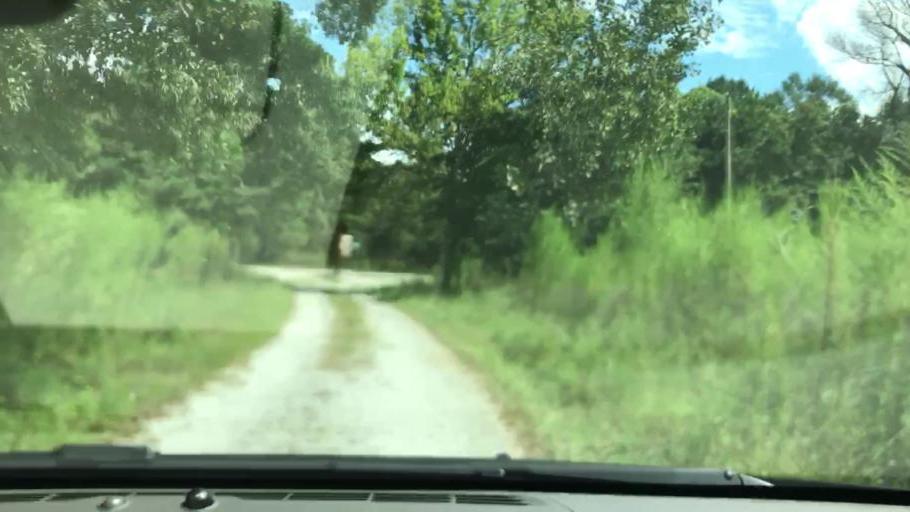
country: US
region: Georgia
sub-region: Quitman County
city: Georgetown
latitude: 31.9952
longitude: -85.0434
